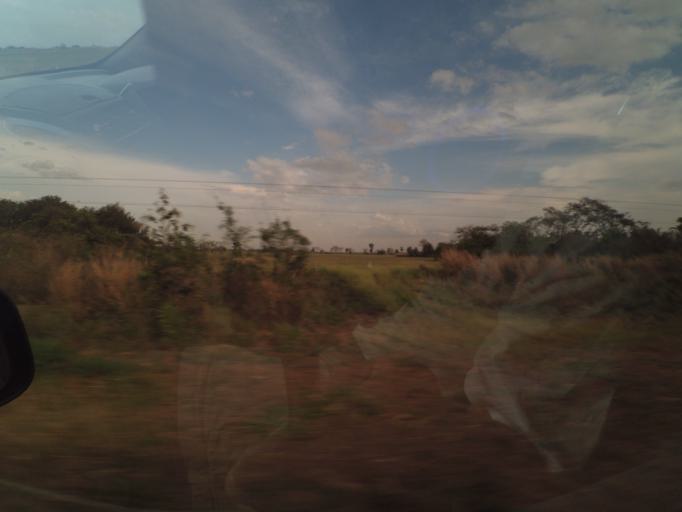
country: BO
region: Santa Cruz
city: Okinawa Numero Uno
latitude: -17.2387
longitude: -62.9687
